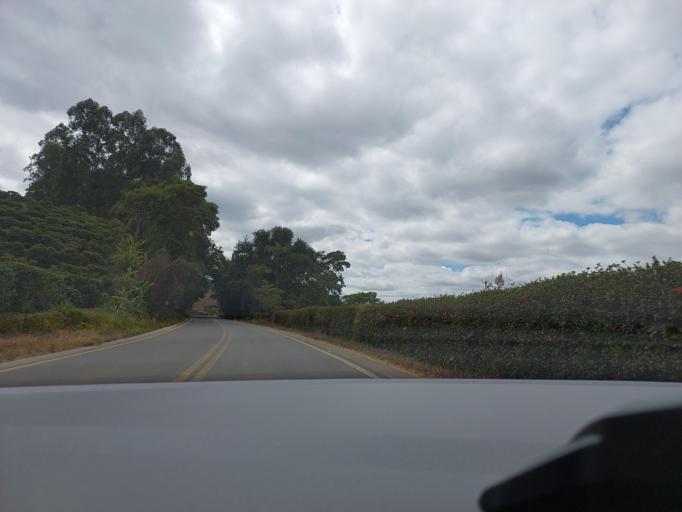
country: BR
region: Minas Gerais
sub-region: Vicosa
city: Vicosa
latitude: -20.8277
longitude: -42.7376
